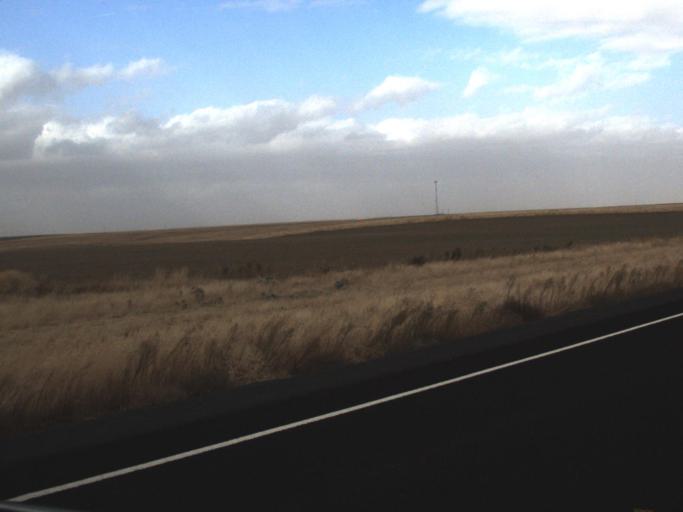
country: US
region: Washington
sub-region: Lincoln County
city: Davenport
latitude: 47.4479
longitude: -118.3182
